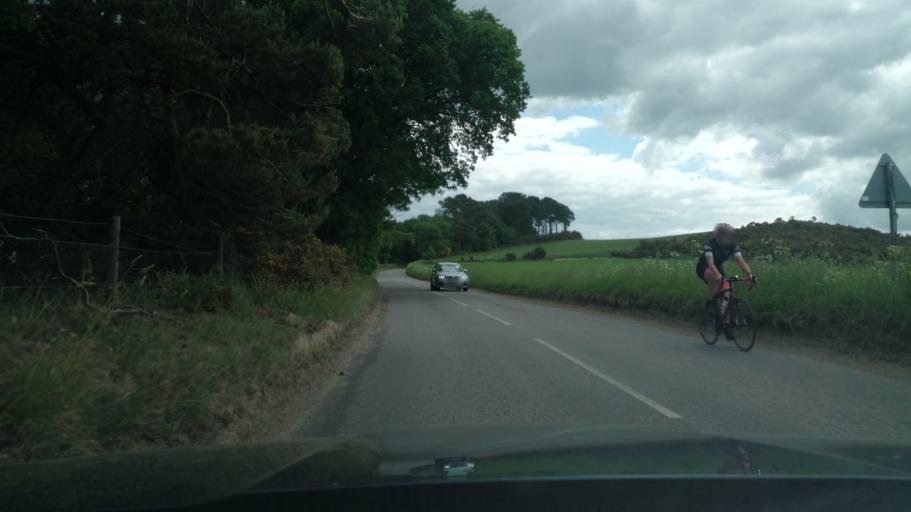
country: GB
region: Scotland
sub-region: Moray
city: Lhanbryd
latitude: 57.6217
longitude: -3.2223
